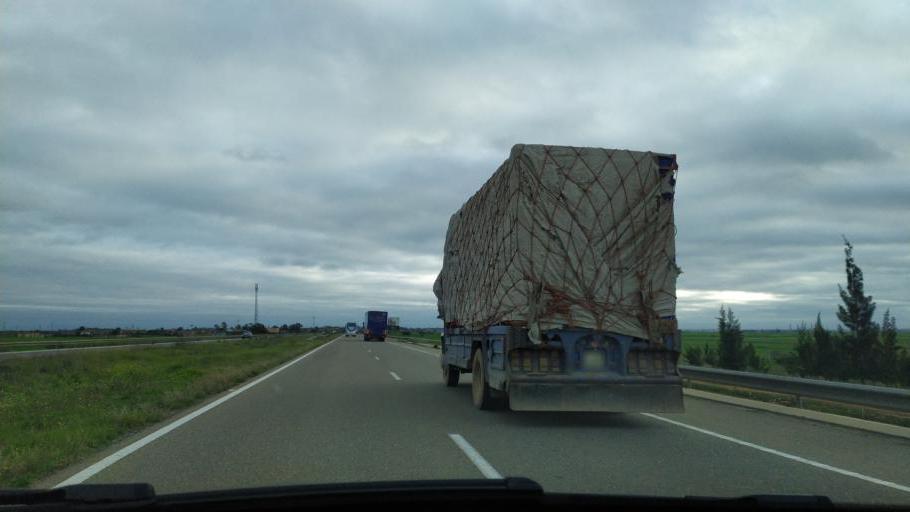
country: MA
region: Gharb-Chrarda-Beni Hssen
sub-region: Kenitra Province
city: Kenitra
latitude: 34.3301
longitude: -6.5102
